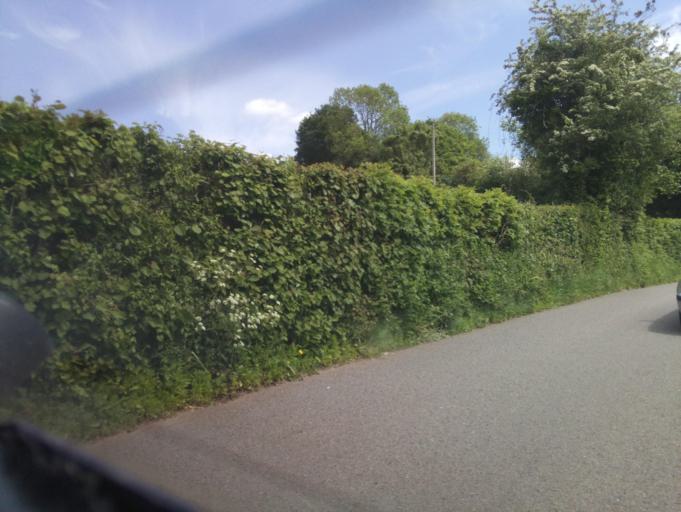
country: GB
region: England
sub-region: Herefordshire
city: Llanrothal
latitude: 51.8733
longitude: -2.8055
